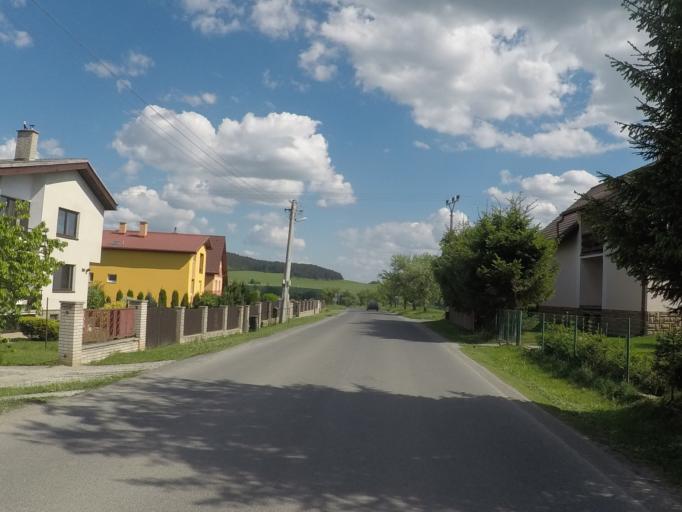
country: SK
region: Presovsky
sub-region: Okres Poprad
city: Poprad
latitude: 49.0172
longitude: 20.3716
